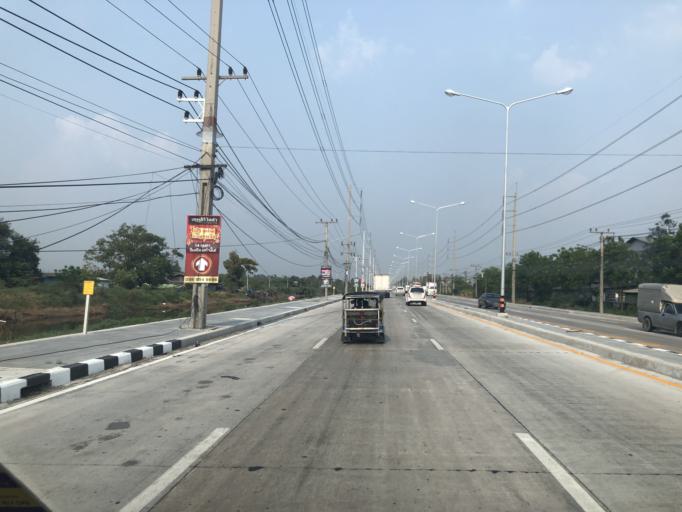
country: TH
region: Chachoengsao
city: Bang Pakong
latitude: 13.4997
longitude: 100.9691
